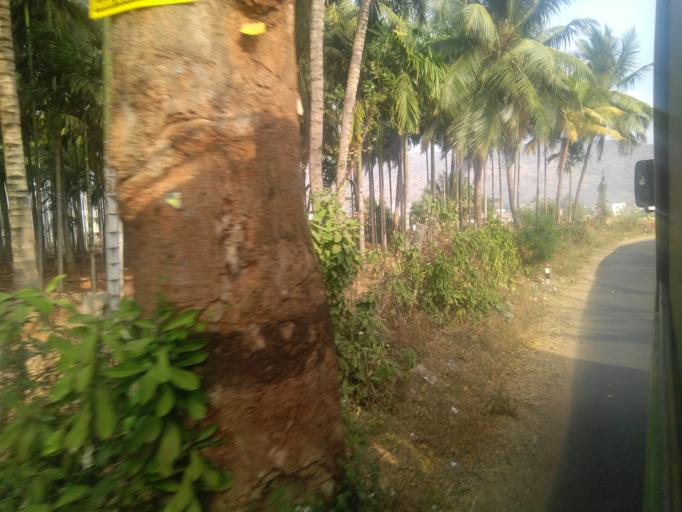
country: IN
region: Tamil Nadu
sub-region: Coimbatore
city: Perur
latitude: 11.0492
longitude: 76.8962
